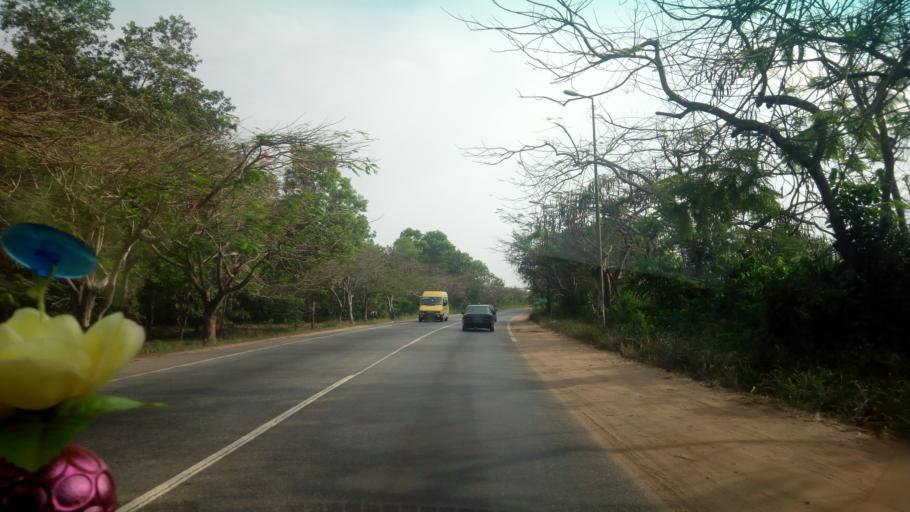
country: GH
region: Central
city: Cape Coast
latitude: 5.1156
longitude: -1.2785
